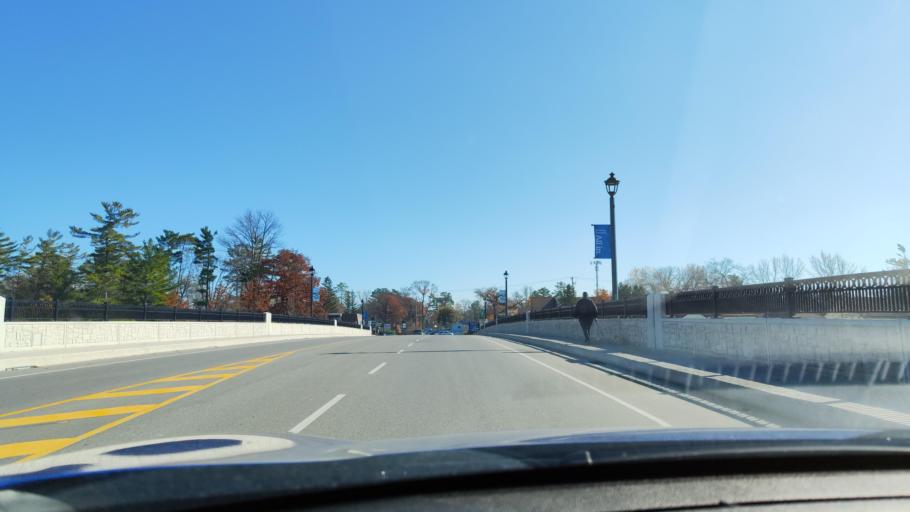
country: CA
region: Ontario
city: Wasaga Beach
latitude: 44.5235
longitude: -80.0177
